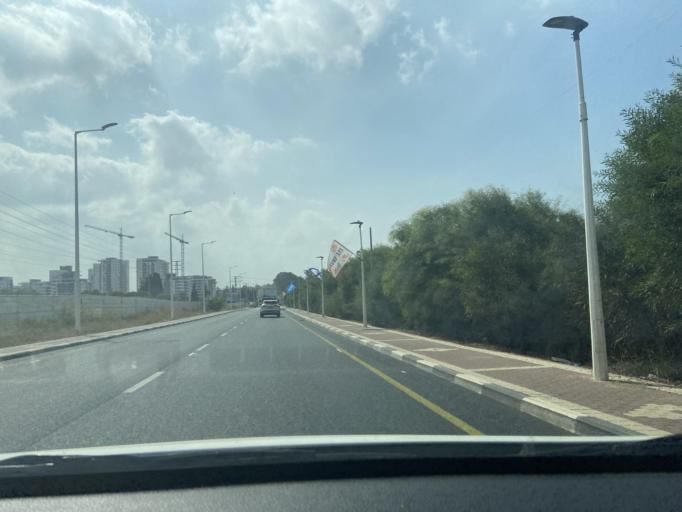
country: IL
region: Northern District
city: Nahariya
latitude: 33.0213
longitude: 35.1036
